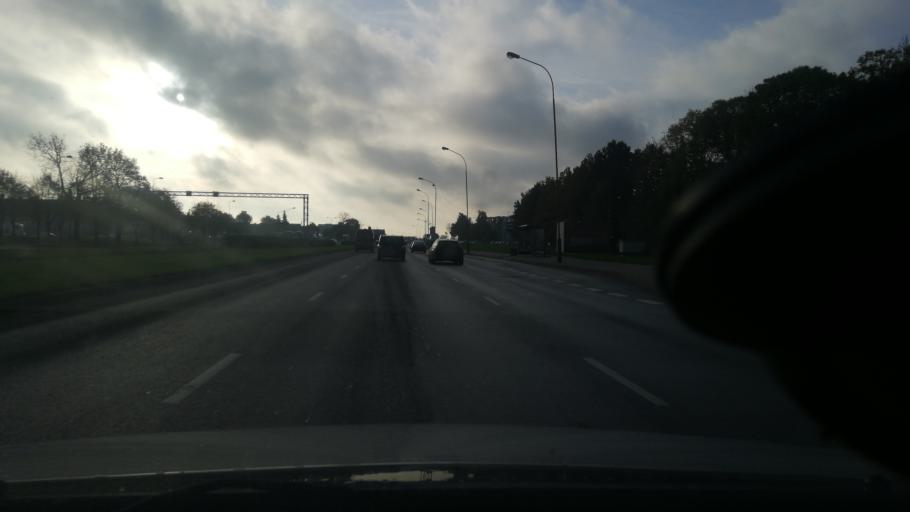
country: LT
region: Klaipedos apskritis
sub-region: Klaipeda
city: Klaipeda
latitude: 55.6912
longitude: 21.1789
